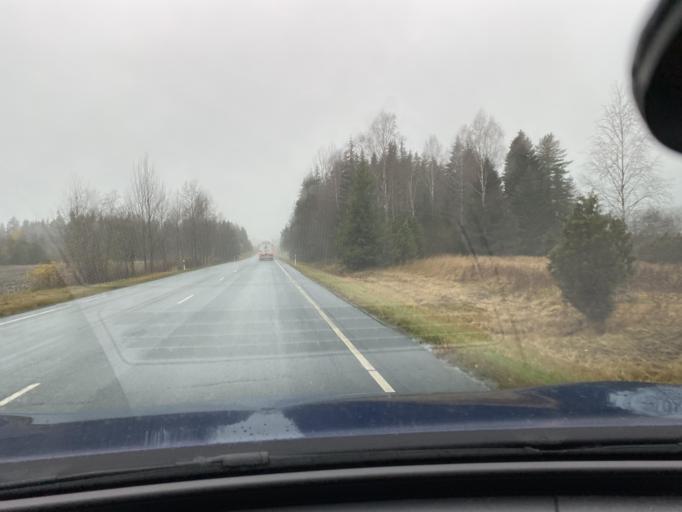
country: FI
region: Haeme
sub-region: Forssa
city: Jokioinen
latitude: 60.7858
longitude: 23.4649
